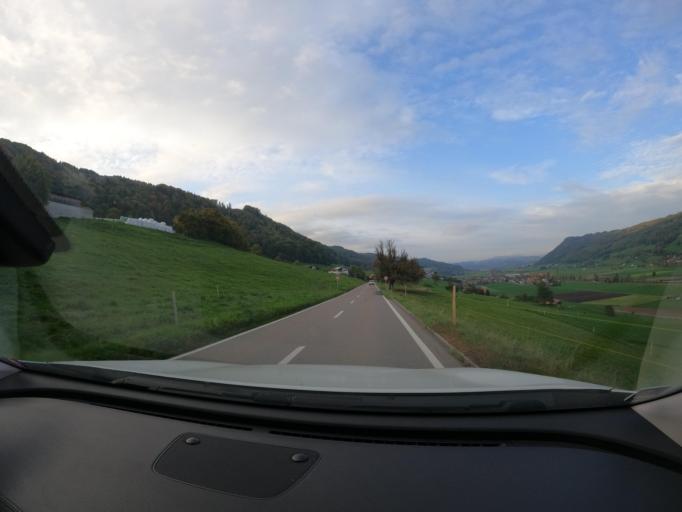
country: CH
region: Bern
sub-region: Bern-Mittelland District
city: Toffen
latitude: 46.8461
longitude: 7.4917
